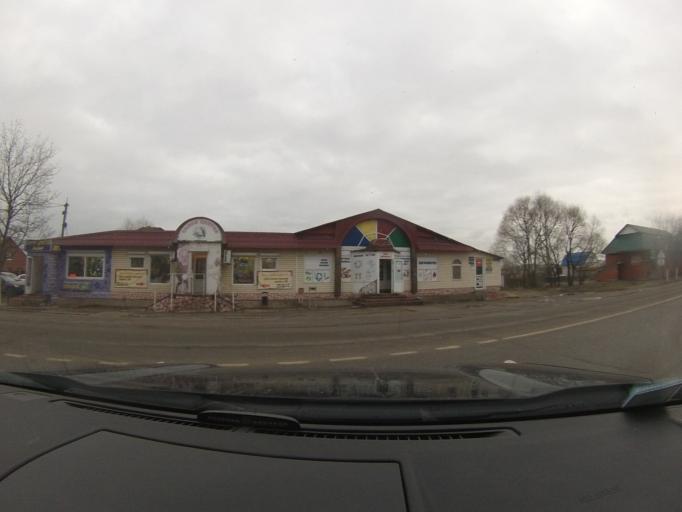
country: RU
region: Moskovskaya
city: Lopatinskiy
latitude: 55.3366
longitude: 38.7135
